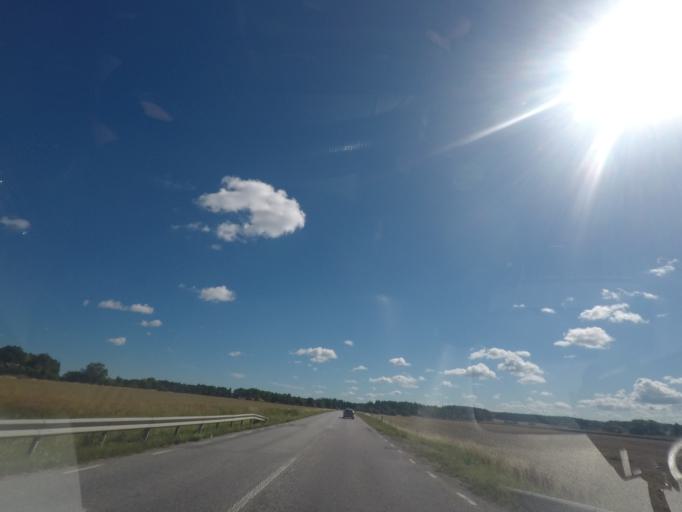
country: SE
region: Uppsala
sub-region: Uppsala Kommun
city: Alsike
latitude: 59.8556
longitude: 17.8404
